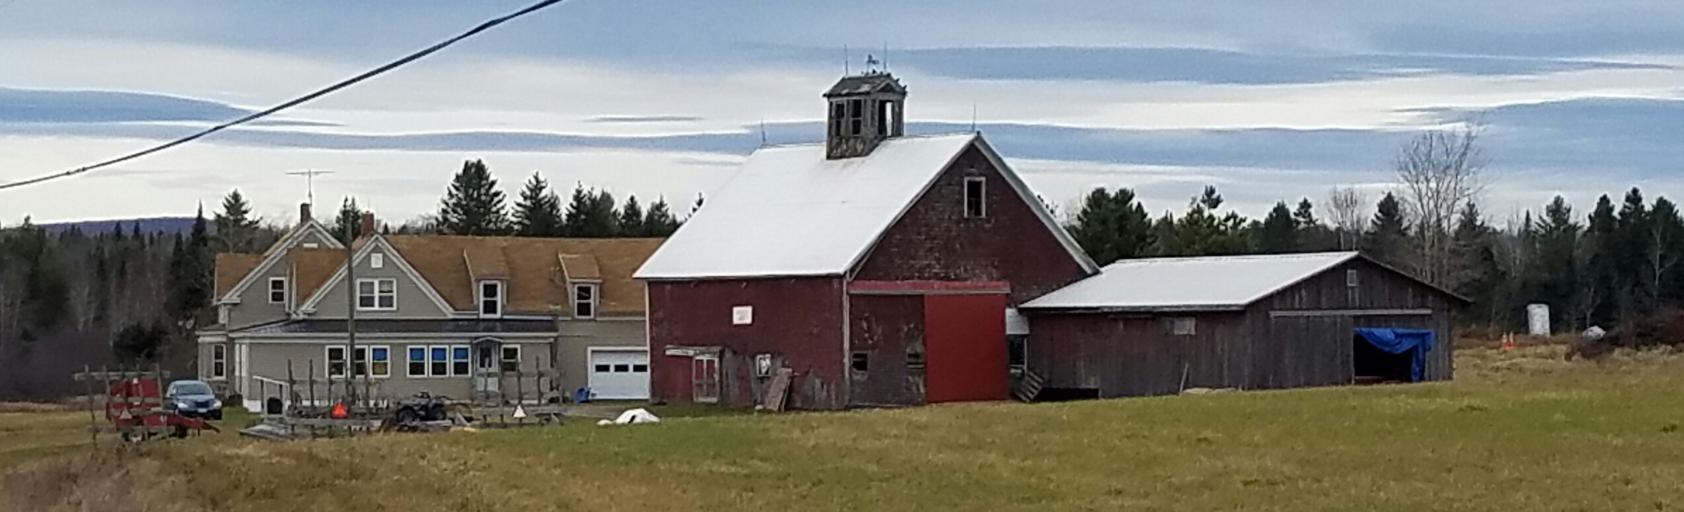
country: US
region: Maine
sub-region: Penobscot County
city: Patten
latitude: 46.1392
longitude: -68.1909
